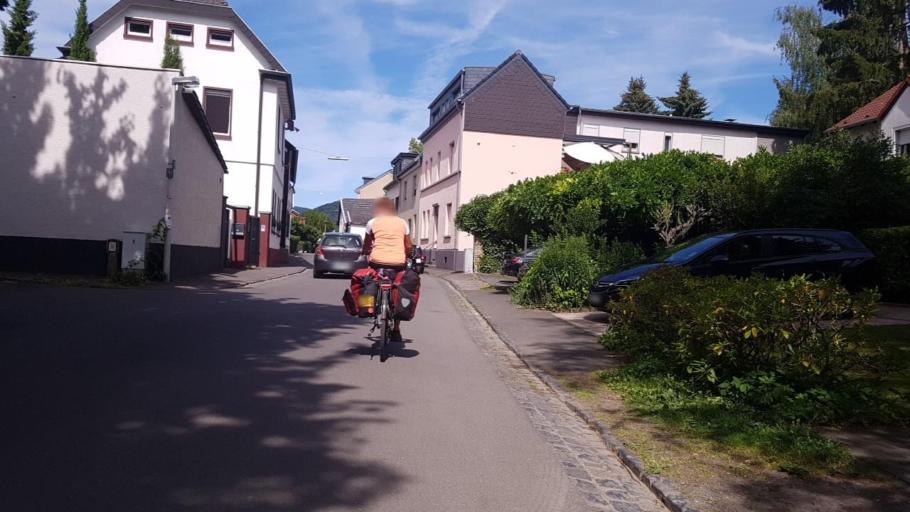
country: DE
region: North Rhine-Westphalia
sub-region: Regierungsbezirk Koln
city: Konigswinter
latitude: 50.6571
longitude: 7.1855
